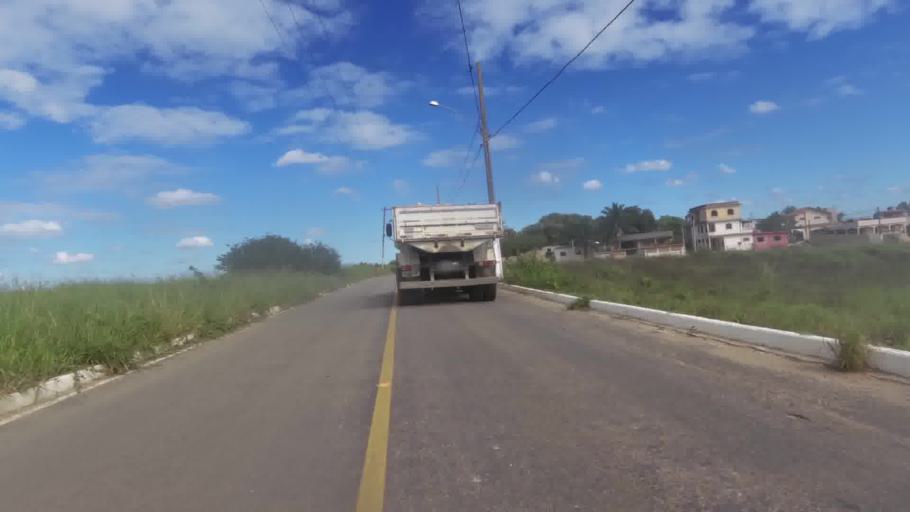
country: BR
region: Espirito Santo
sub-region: Marataizes
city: Marataizes
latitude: -21.0527
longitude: -40.8379
